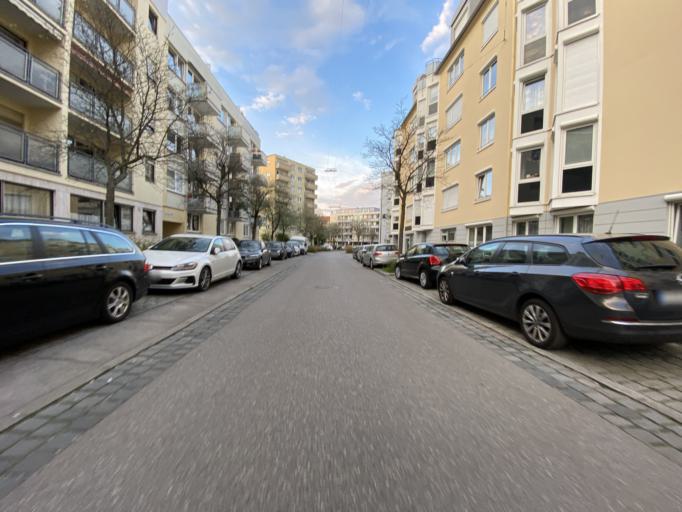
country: DE
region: Bavaria
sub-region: Upper Bavaria
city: Munich
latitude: 48.1588
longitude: 11.5428
